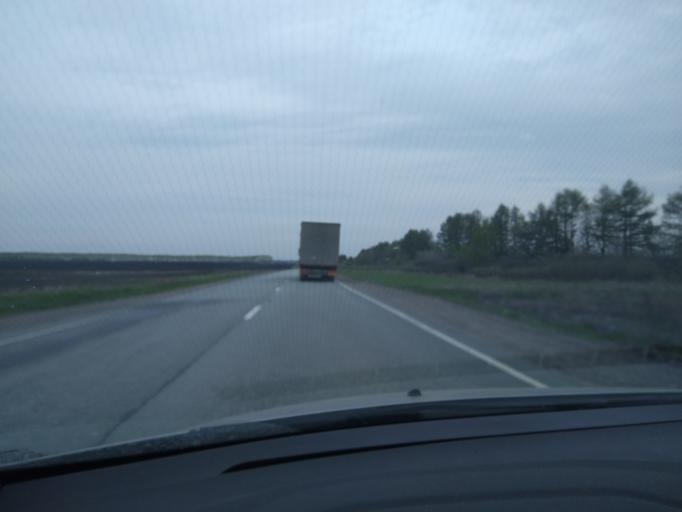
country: RU
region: Sverdlovsk
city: Yelanskiy
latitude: 56.7700
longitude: 62.4390
